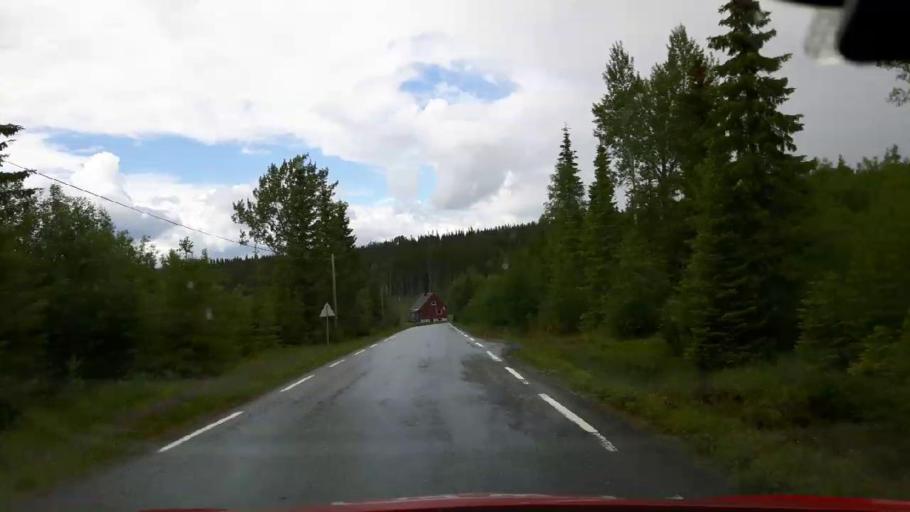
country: NO
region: Nord-Trondelag
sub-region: Lierne
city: Sandvika
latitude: 64.1010
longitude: 14.0242
